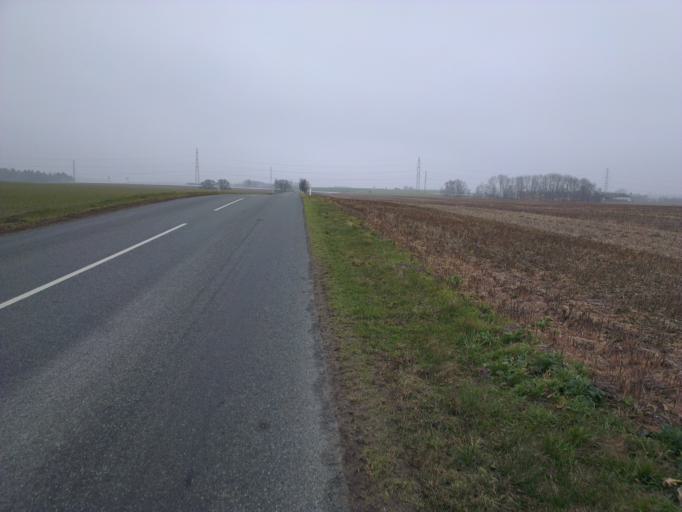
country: DK
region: Capital Region
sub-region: Frederikssund Kommune
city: Frederikssund
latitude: 55.8047
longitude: 12.0223
